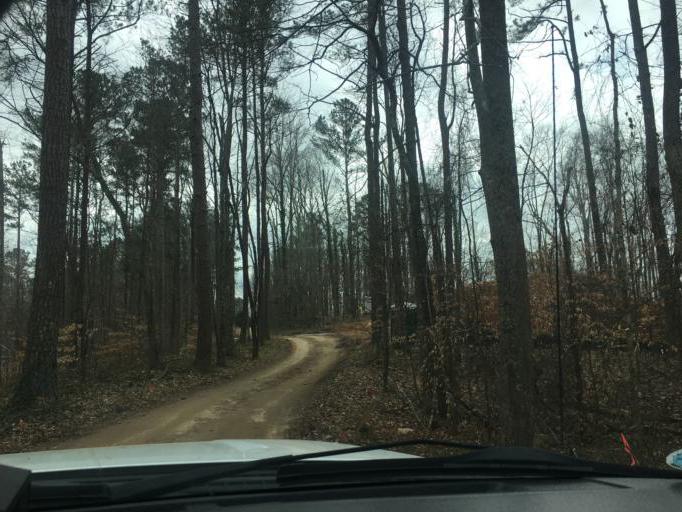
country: US
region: Georgia
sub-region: Fulton County
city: Milton
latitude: 34.2083
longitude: -84.3138
